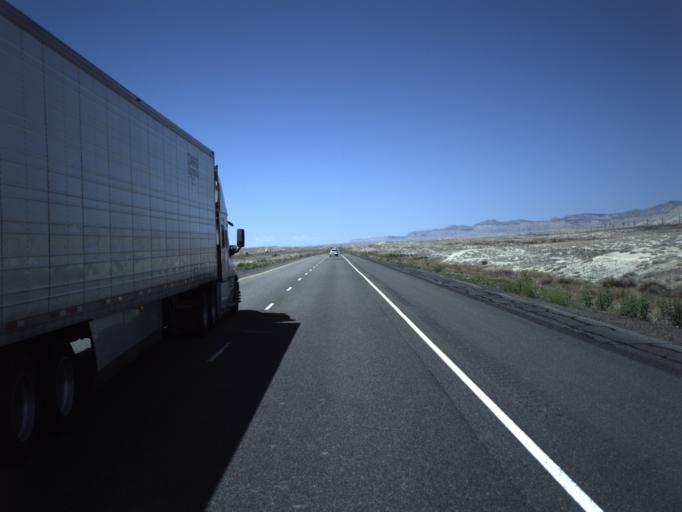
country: US
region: Utah
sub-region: Grand County
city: Moab
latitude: 38.9350
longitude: -109.4528
